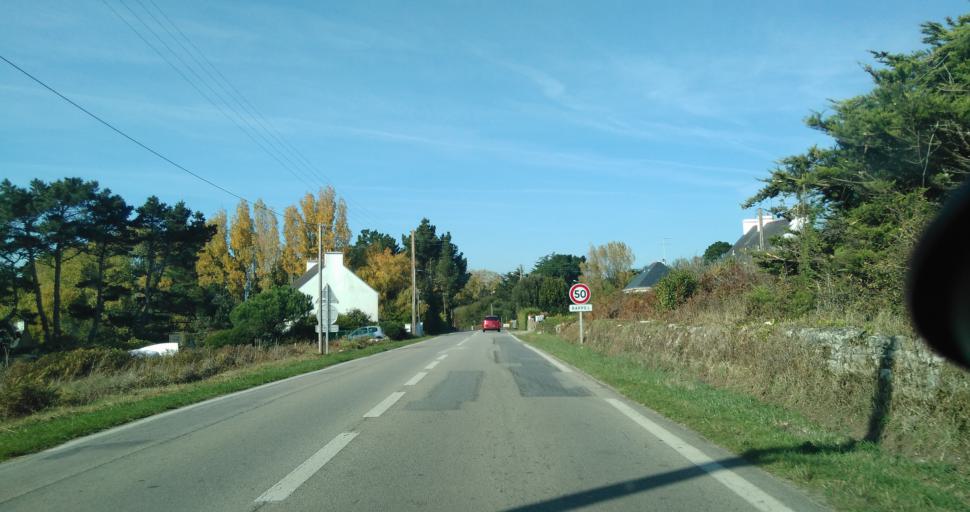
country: FR
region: Brittany
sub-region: Departement du Morbihan
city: Plouharnel
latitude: 47.5974
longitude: -3.1226
